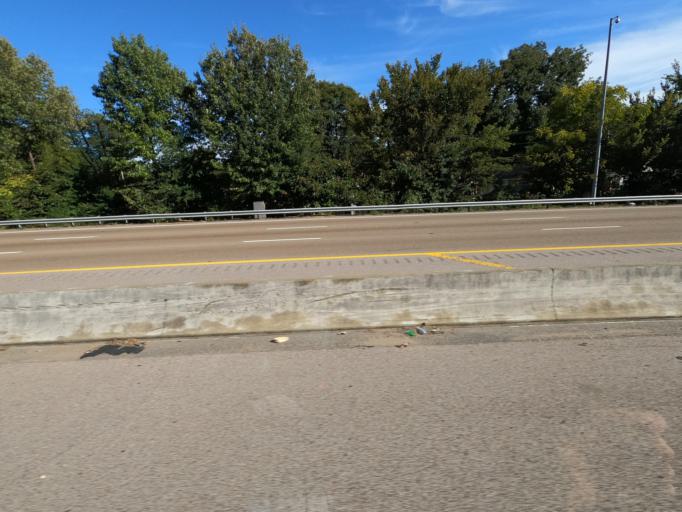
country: US
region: Tennessee
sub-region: Shelby County
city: Memphis
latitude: 35.1179
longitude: -90.0265
